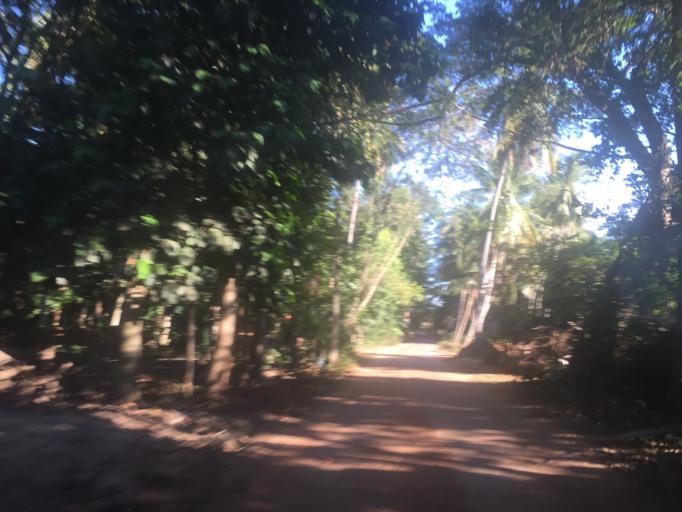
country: TH
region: Changwat Udon Thani
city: Si That
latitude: 16.9697
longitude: 103.2289
